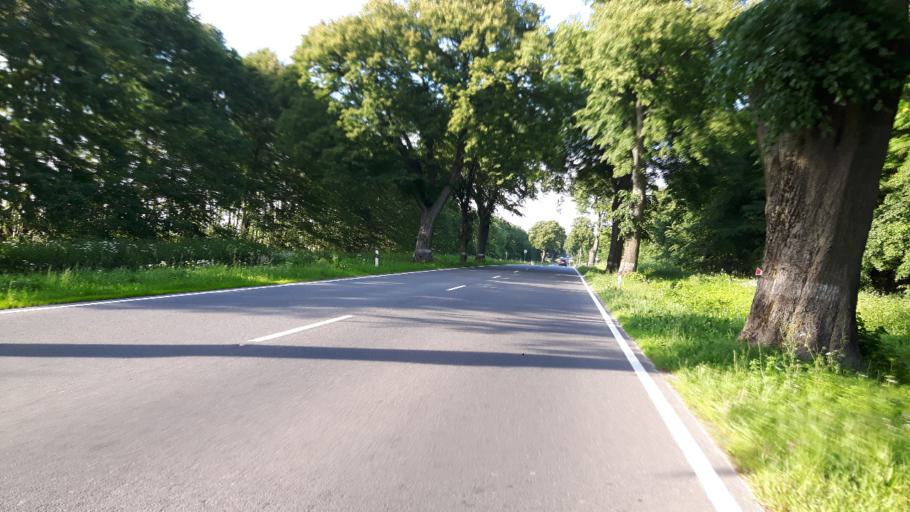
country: RU
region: Kaliningrad
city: Ladushkin
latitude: 54.5083
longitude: 20.1025
